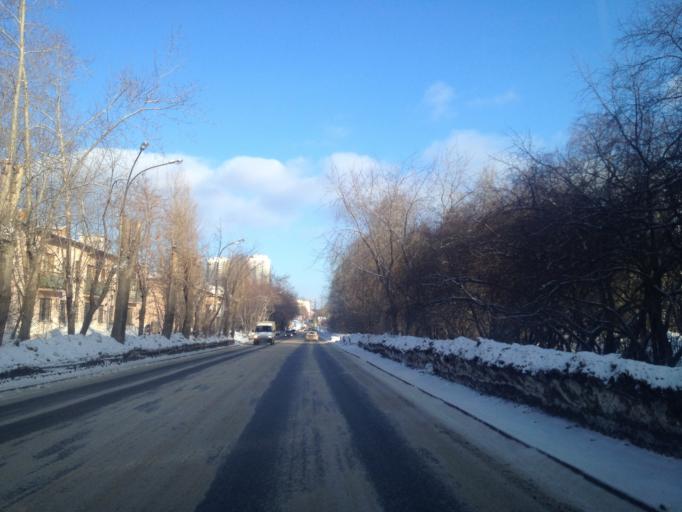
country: RU
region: Sverdlovsk
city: Sovkhoznyy
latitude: 56.7688
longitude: 60.6023
